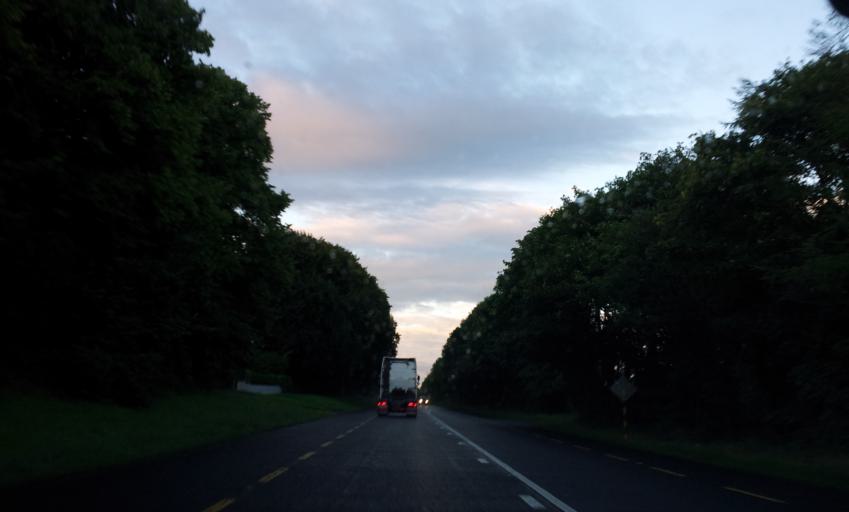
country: IE
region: Munster
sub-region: County Limerick
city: Adare
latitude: 52.5467
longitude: -8.8328
